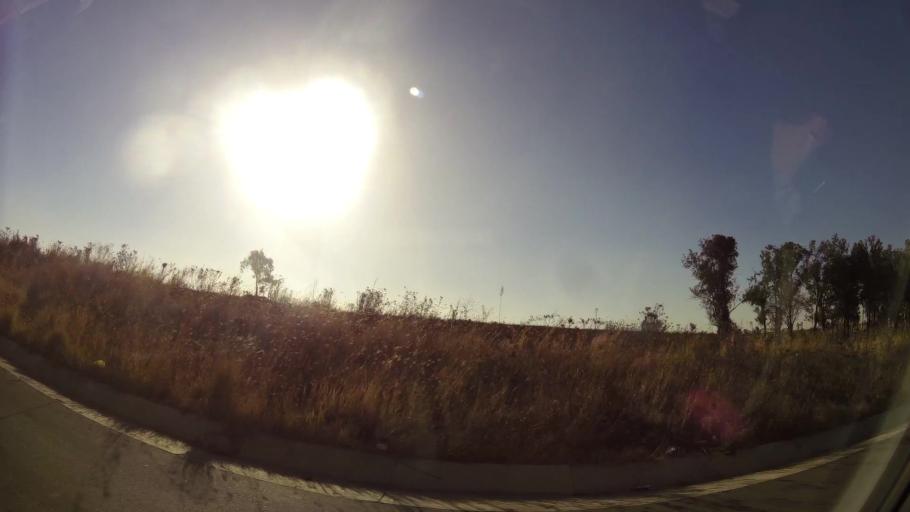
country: ZA
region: Gauteng
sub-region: City of Johannesburg Metropolitan Municipality
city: Diepsloot
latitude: -25.9441
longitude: 27.9751
